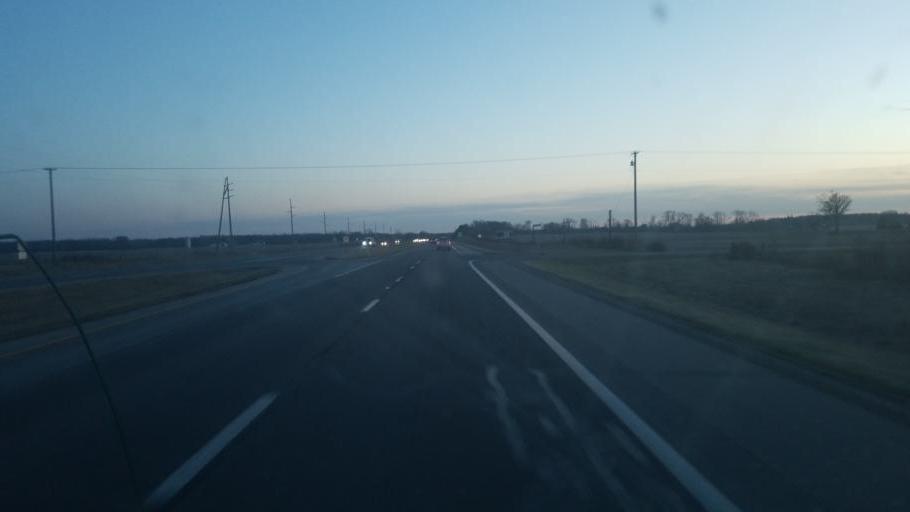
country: US
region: Ohio
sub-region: Marion County
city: Marion
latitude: 40.4848
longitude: -83.0748
